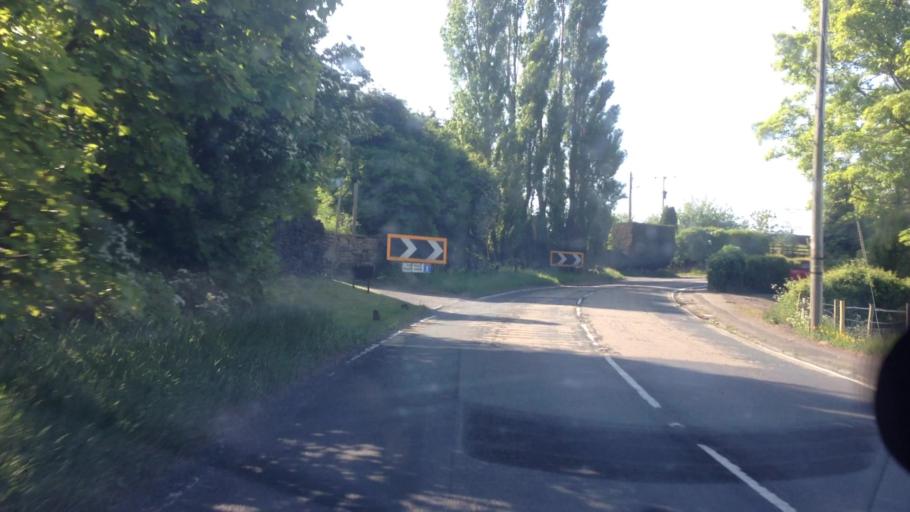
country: GB
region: England
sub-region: Kirklees
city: Mirfield
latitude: 53.6742
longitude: -1.7282
